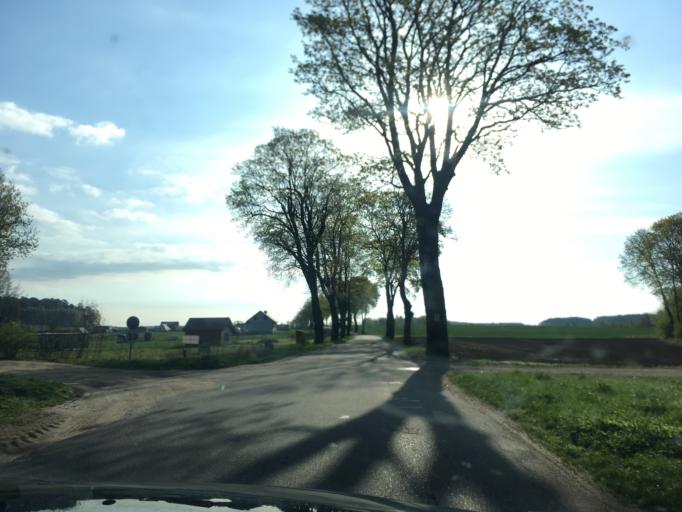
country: PL
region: Warmian-Masurian Voivodeship
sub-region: Powiat nidzicki
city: Kozlowo
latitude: 53.4046
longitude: 20.2819
